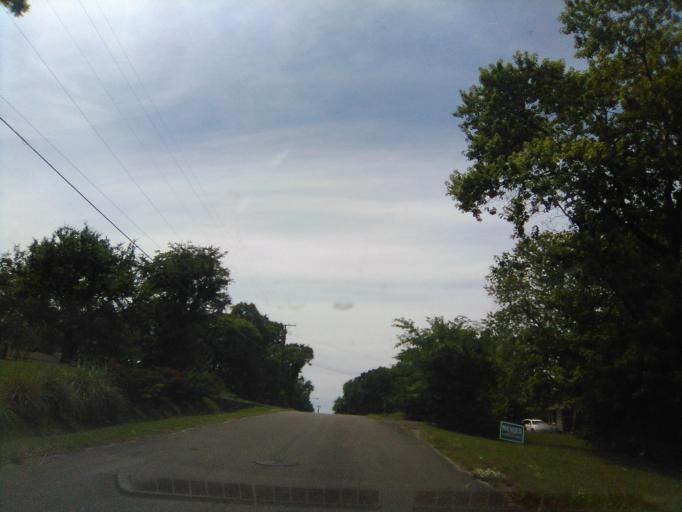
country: US
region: Tennessee
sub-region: Davidson County
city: Belle Meade
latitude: 36.1250
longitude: -86.8961
